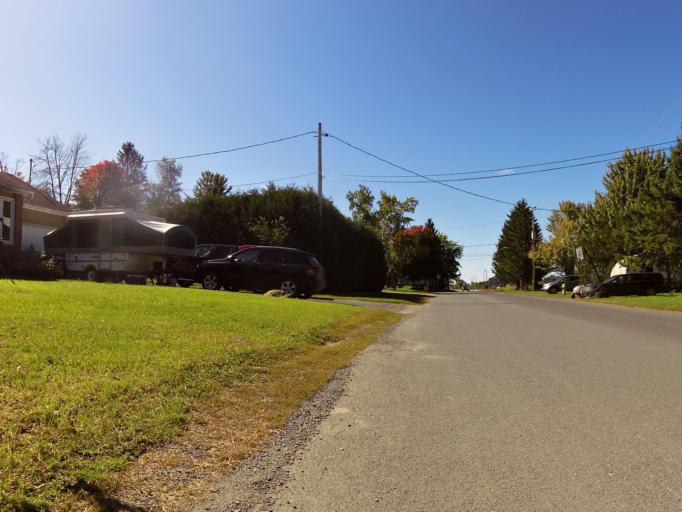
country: CA
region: Ontario
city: Casselman
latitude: 45.2665
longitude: -75.2790
